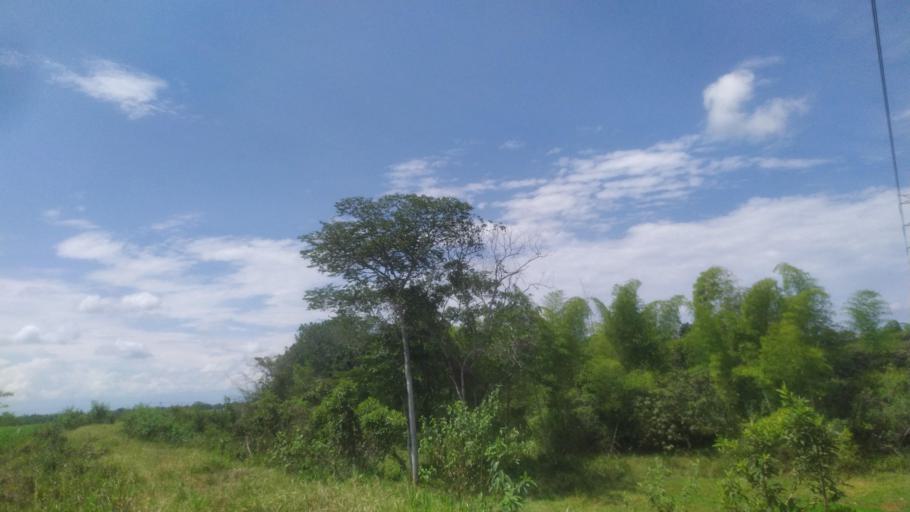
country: CO
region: Valle del Cauca
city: Jamundi
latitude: 3.2842
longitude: -76.5327
